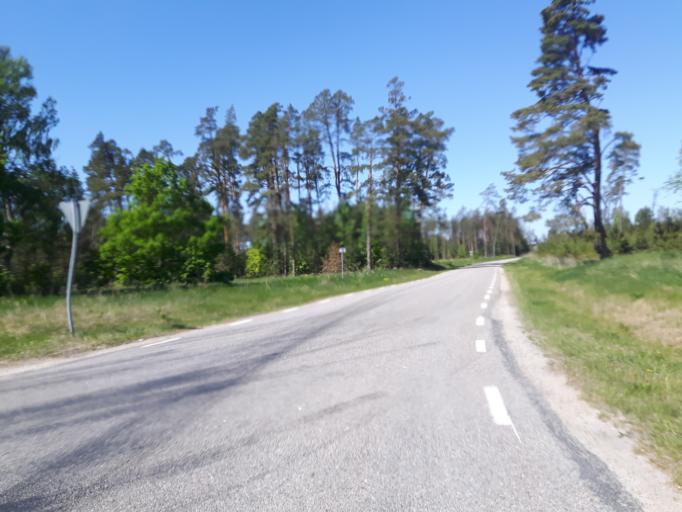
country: EE
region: Laeaene-Virumaa
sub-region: Viru-Nigula vald
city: Kunda
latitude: 59.4974
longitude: 26.4840
